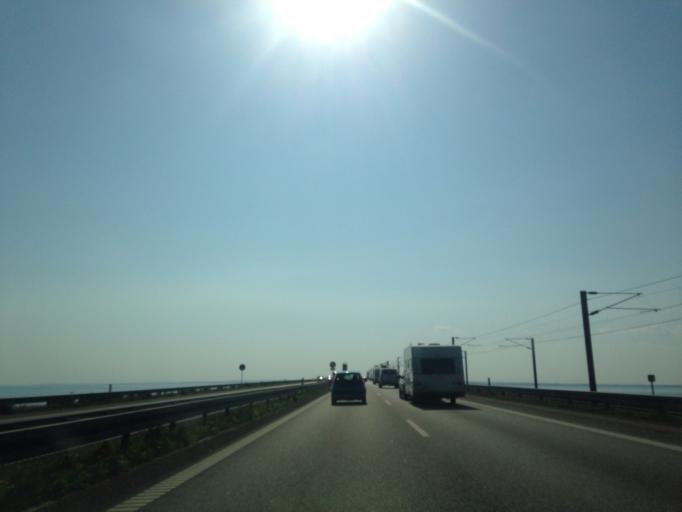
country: DK
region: South Denmark
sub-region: Nyborg Kommune
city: Nyborg
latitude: 55.3273
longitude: 10.9505
